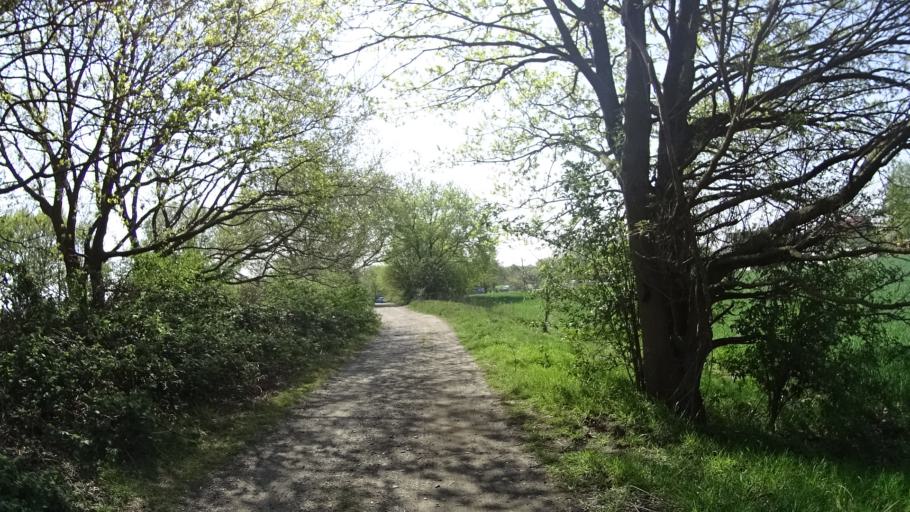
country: DE
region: North Rhine-Westphalia
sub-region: Regierungsbezirk Dusseldorf
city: Moers
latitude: 51.3910
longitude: 6.6291
